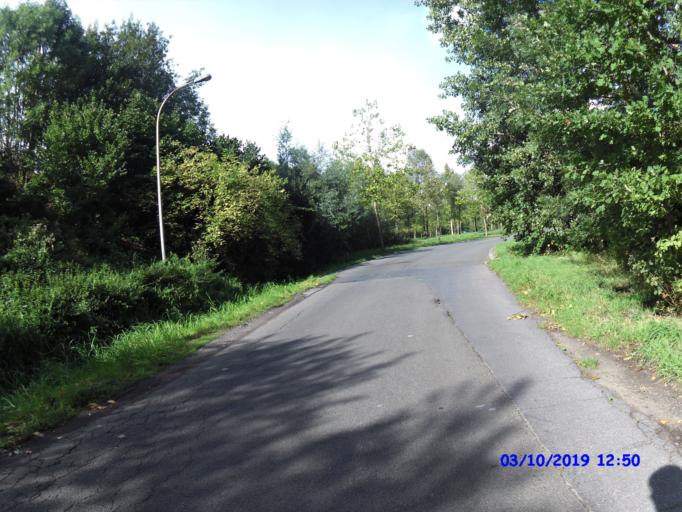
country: BE
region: Flanders
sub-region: Provincie Oost-Vlaanderen
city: Denderleeuw
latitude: 50.8867
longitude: 4.0818
